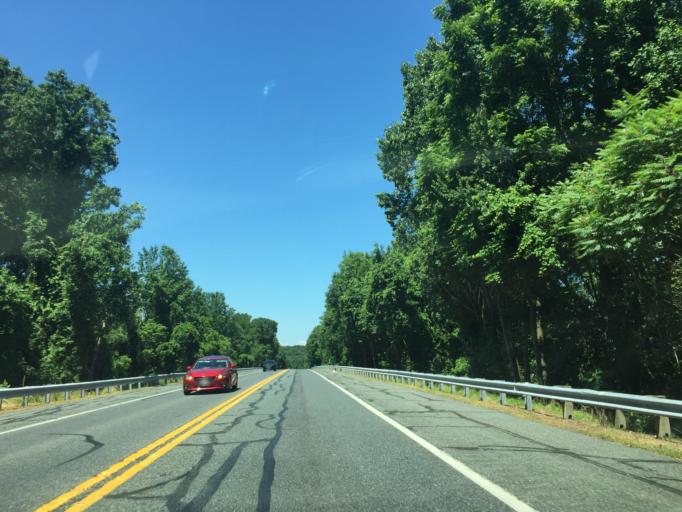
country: US
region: Maryland
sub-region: Harford County
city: Jarrettsville
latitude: 39.5751
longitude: -76.4281
